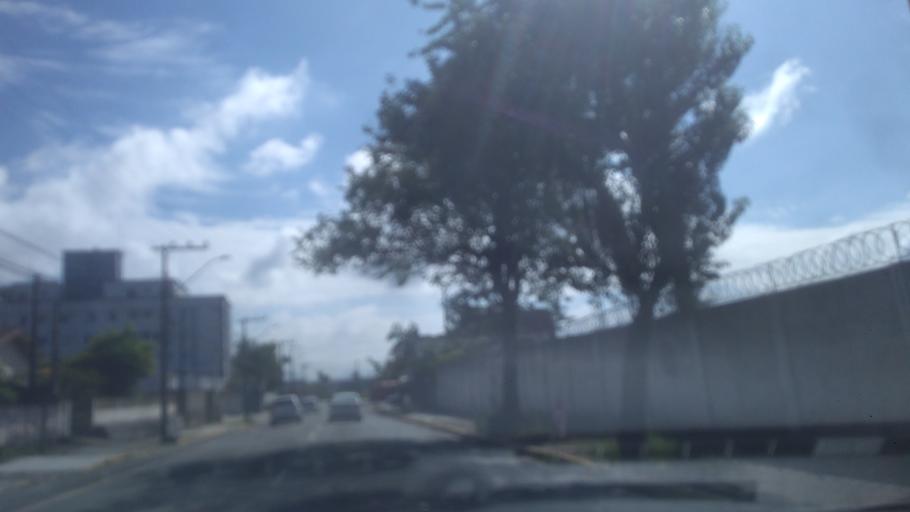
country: BR
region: Santa Catarina
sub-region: Joinville
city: Joinville
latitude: -26.3095
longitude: -48.8289
